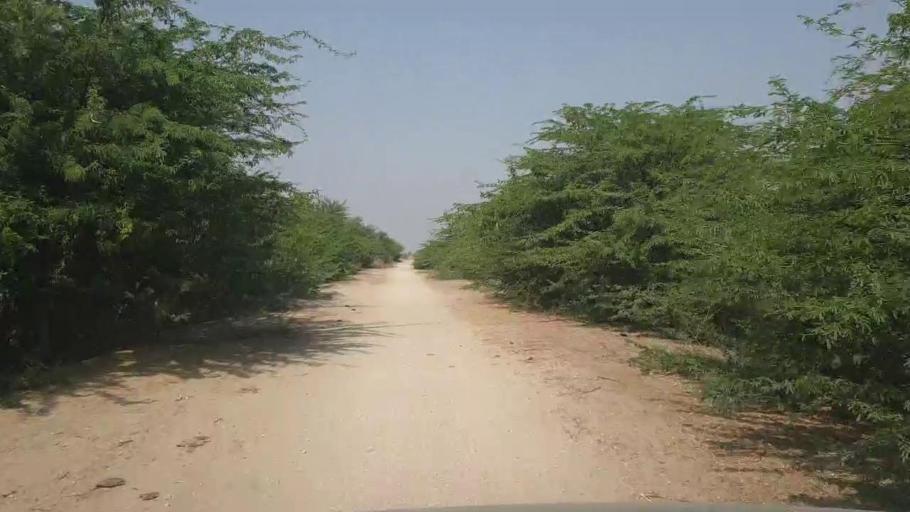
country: PK
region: Sindh
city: Chor
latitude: 25.4659
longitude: 69.7654
